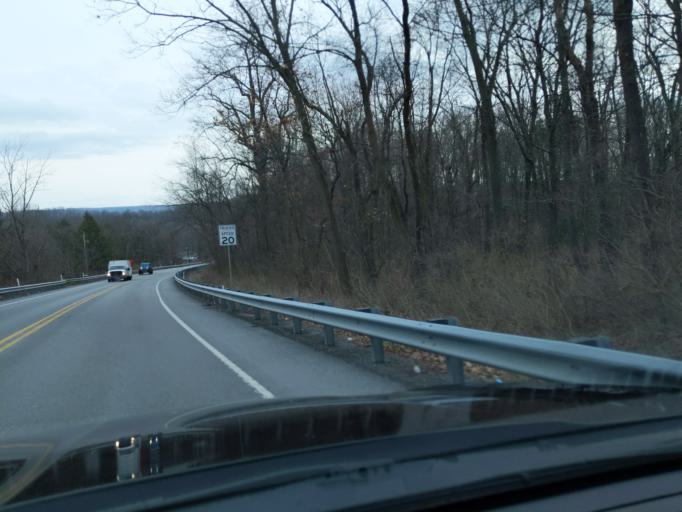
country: US
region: Pennsylvania
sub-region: Blair County
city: Lakemont
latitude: 40.4598
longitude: -78.3589
